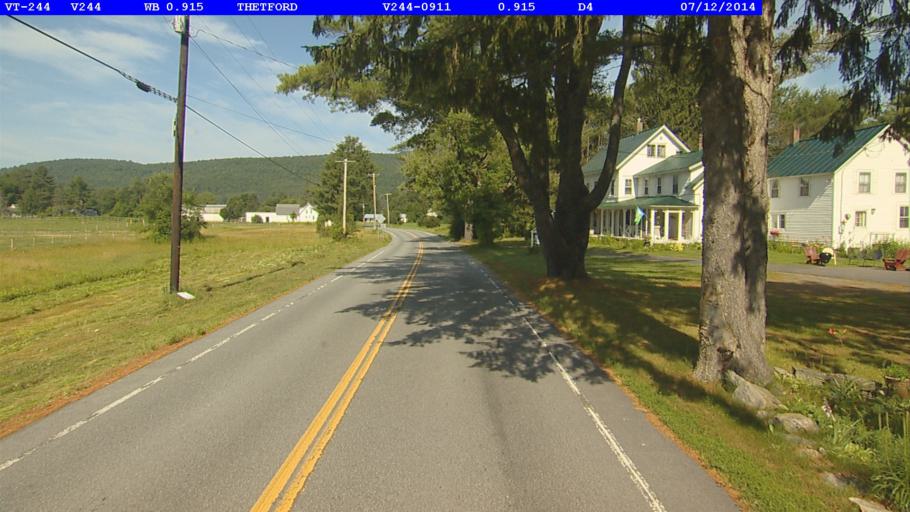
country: US
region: New Hampshire
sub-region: Grafton County
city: Orford
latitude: 43.8880
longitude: -72.2428
